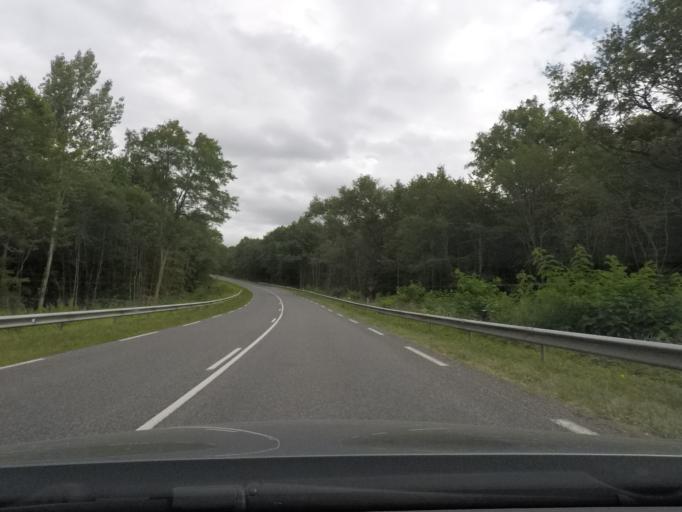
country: FR
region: Auvergne
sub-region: Departement de l'Allier
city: Brugheas
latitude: 46.0637
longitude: 3.3784
